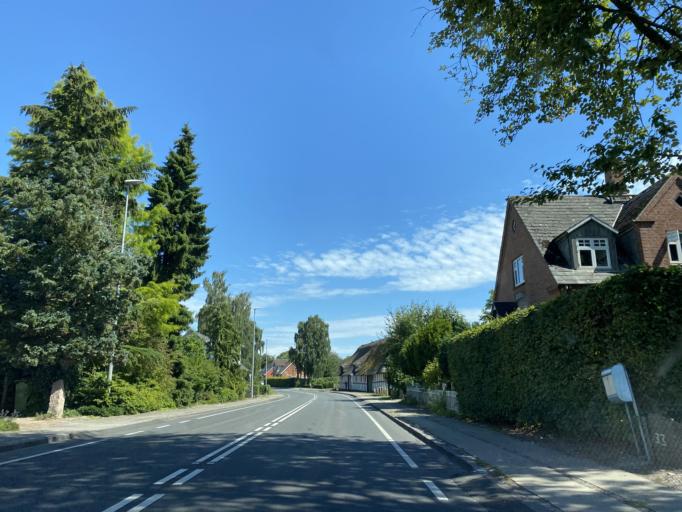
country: DK
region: South Denmark
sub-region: Faaborg-Midtfyn Kommune
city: Ringe
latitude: 55.2446
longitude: 10.5435
